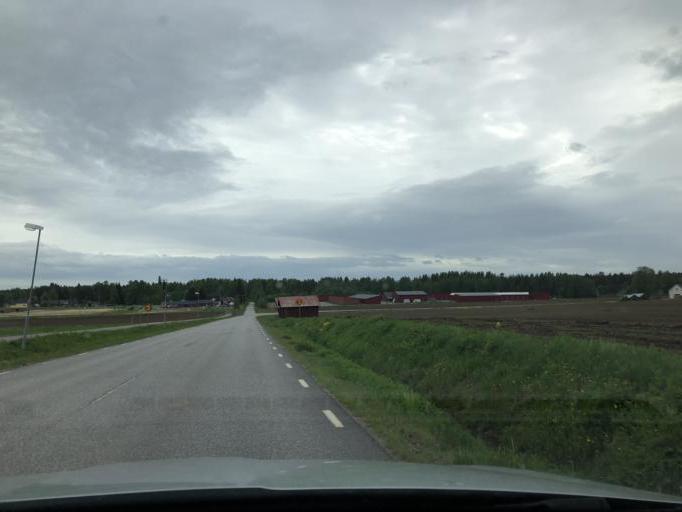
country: SE
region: Norrbotten
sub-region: Pitea Kommun
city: Bergsviken
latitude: 65.3824
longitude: 21.3136
